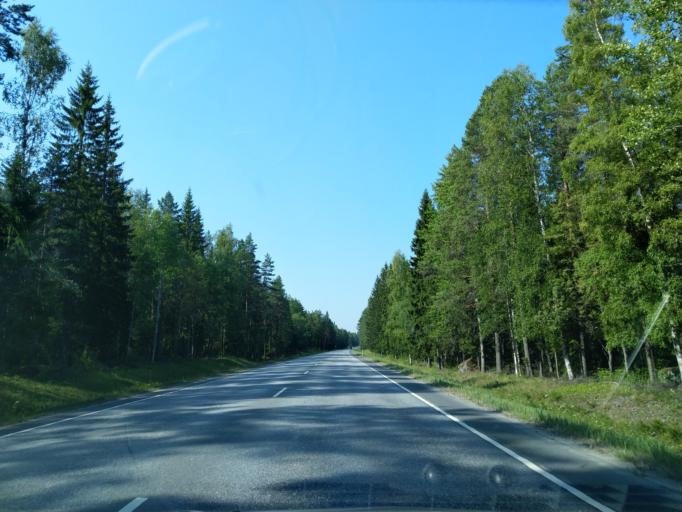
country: FI
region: Satakunta
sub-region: Pori
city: Noormarkku
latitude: 61.6275
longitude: 21.9239
